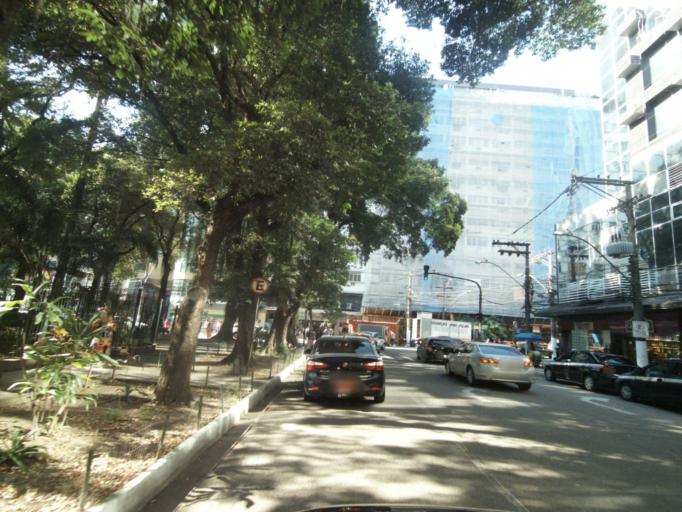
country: BR
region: Rio de Janeiro
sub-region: Niteroi
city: Niteroi
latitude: -22.8947
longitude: -43.1209
